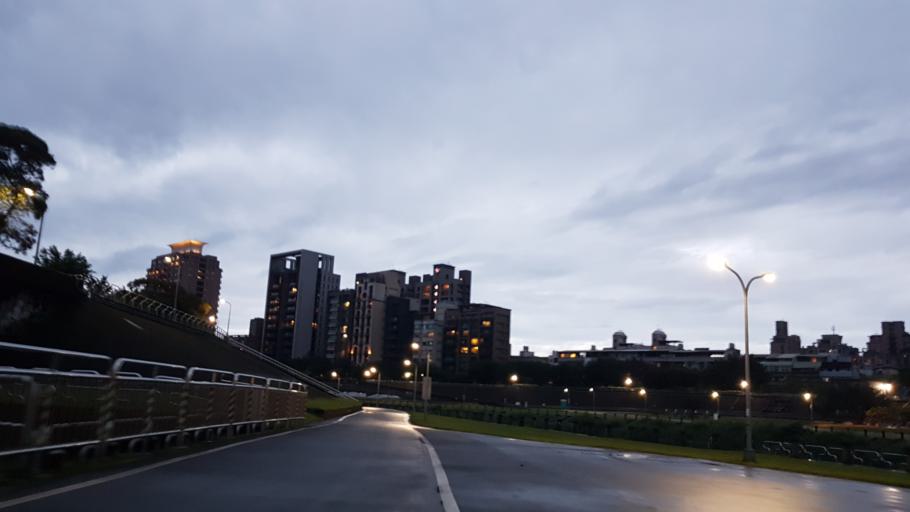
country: TW
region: Taipei
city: Taipei
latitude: 24.9802
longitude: 121.5664
